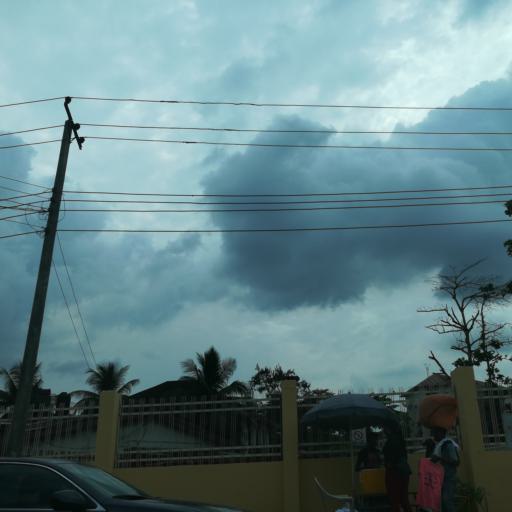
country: NG
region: Rivers
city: Port Harcourt
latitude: 4.8280
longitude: 6.9980
